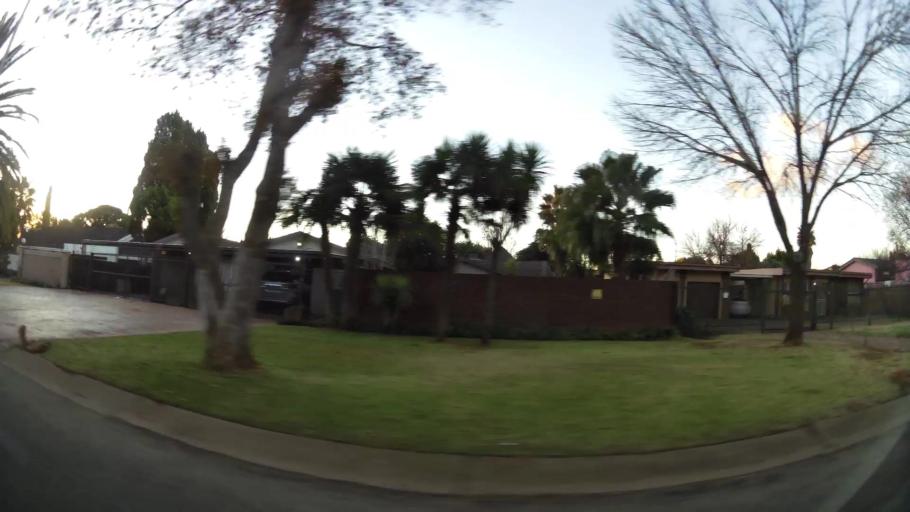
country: ZA
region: North-West
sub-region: Dr Kenneth Kaunda District Municipality
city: Potchefstroom
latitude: -26.7227
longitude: 27.1136
